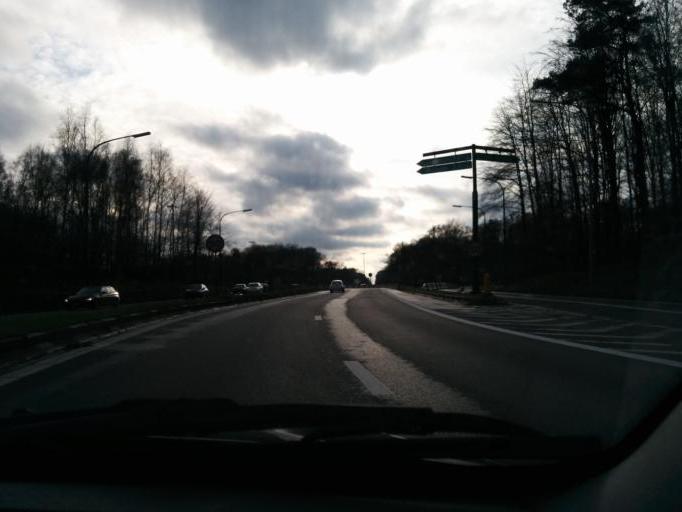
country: BE
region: Flanders
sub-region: Provincie Vlaams-Brabant
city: Hoeilaart
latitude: 50.8023
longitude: 4.4658
